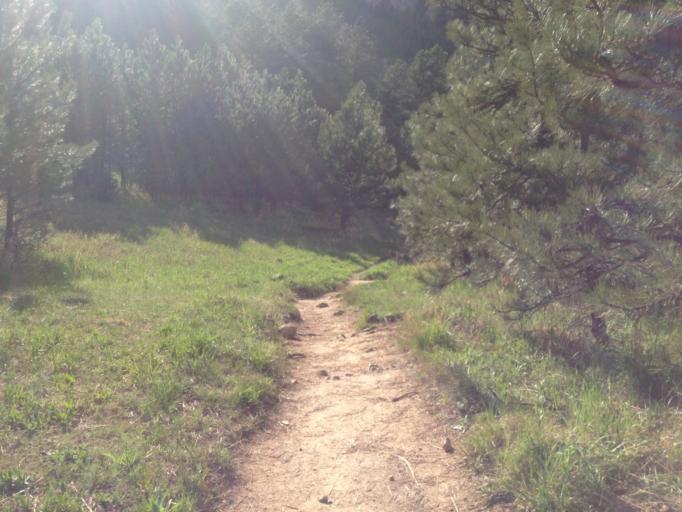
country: US
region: Colorado
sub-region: Boulder County
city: Boulder
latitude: 39.9492
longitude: -105.2793
